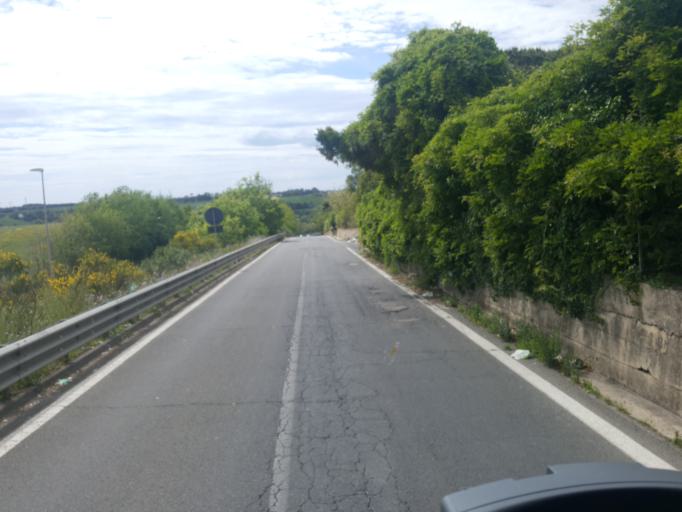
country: IT
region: Latium
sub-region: Citta metropolitana di Roma Capitale
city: La Massimina-Casal Lumbroso
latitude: 41.8823
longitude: 12.3461
